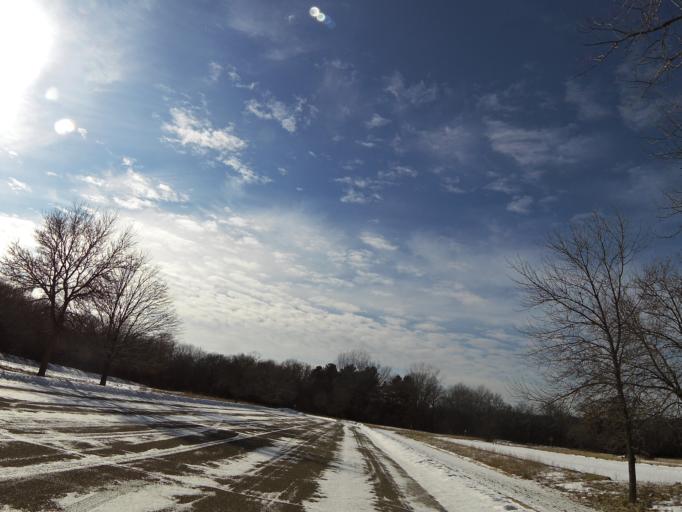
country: US
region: Wisconsin
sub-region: Saint Croix County
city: North Hudson
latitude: 45.0129
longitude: -92.7045
